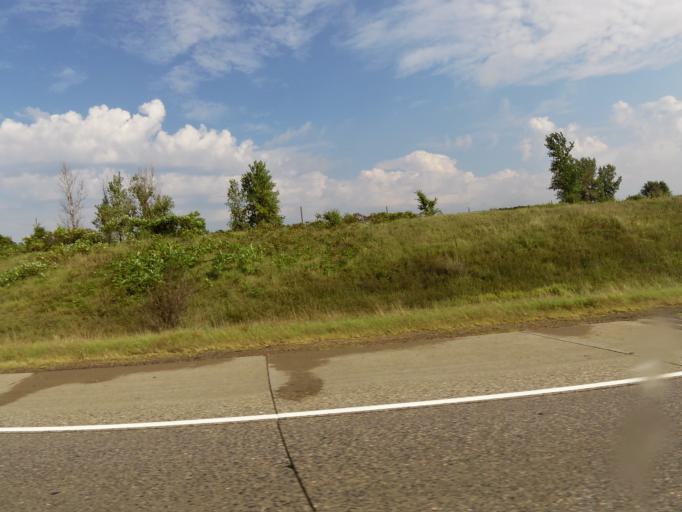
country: US
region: Minnesota
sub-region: Washington County
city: Lake Elmo
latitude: 44.9488
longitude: -92.8853
